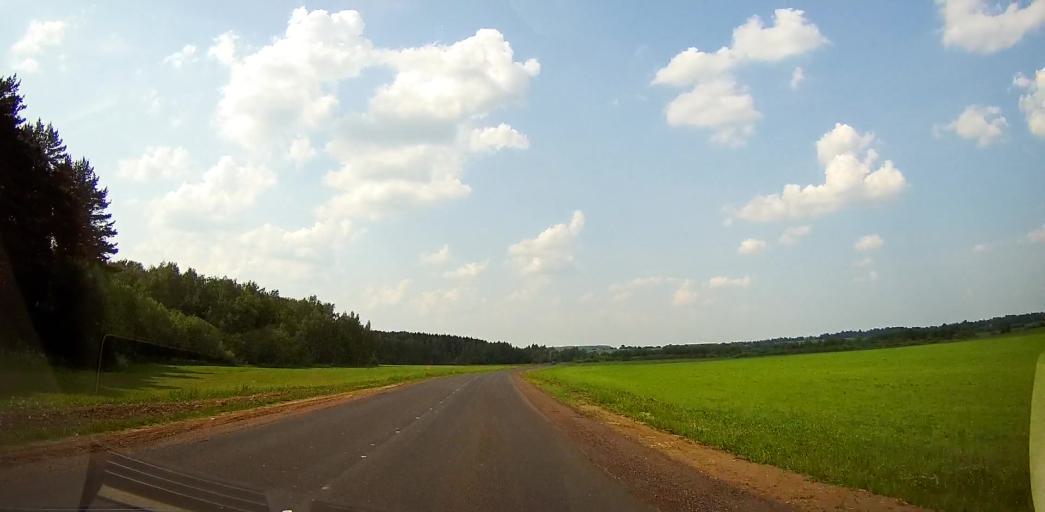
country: RU
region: Moskovskaya
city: Malino
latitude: 55.0601
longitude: 38.1459
